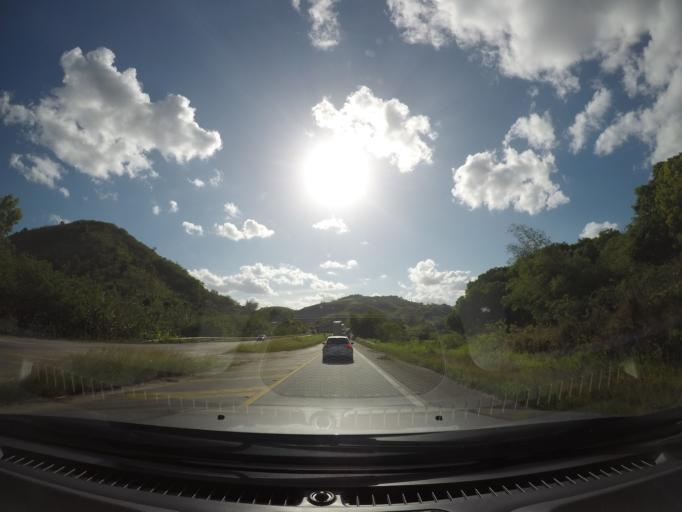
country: BR
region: Alagoas
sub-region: Flexeiras
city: Flexeiras
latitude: -9.0927
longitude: -35.7501
